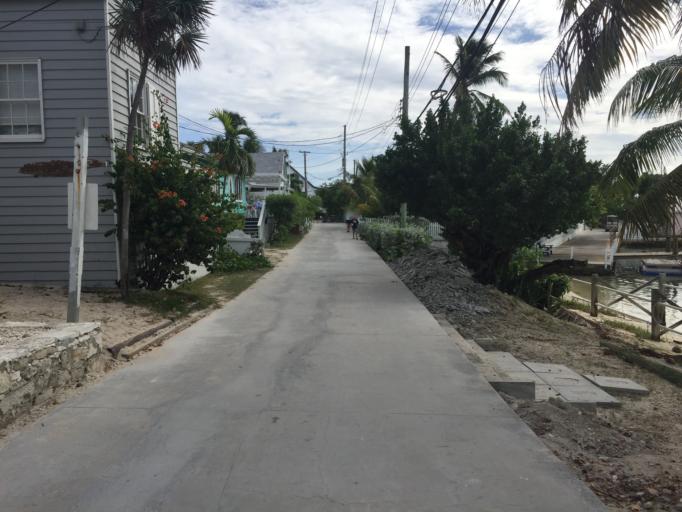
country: BS
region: Central Abaco
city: Marsh Harbour
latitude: 26.5386
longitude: -76.9575
